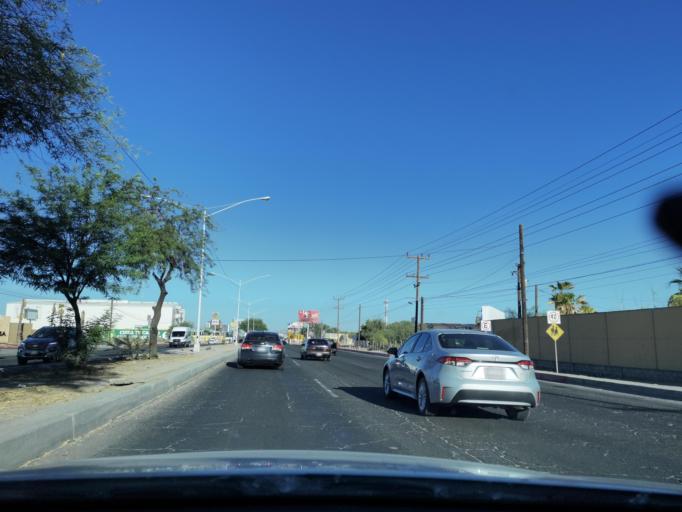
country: MX
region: Baja California
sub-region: Mexicali
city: Islas Agrarias Grupo A
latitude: 32.6530
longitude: -115.3721
